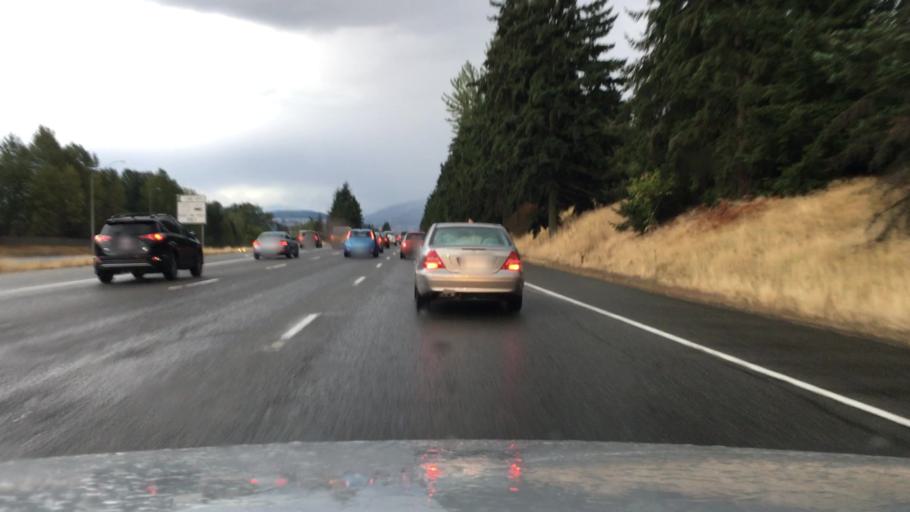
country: US
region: Washington
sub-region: King County
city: Eastgate
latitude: 47.5767
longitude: -122.1287
